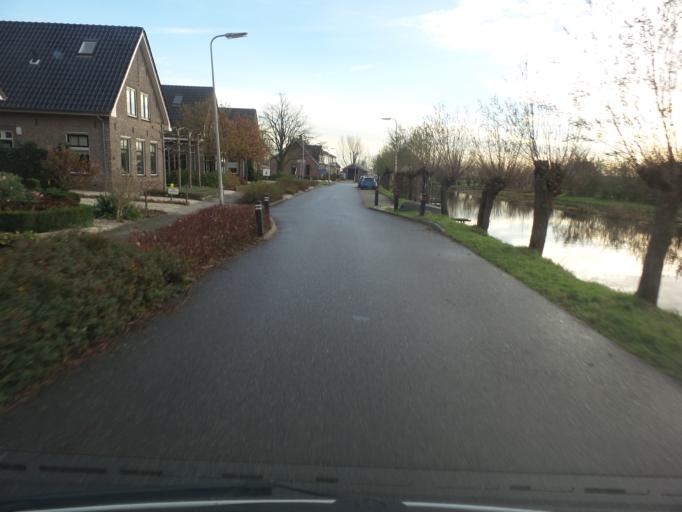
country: NL
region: Utrecht
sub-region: Gemeente Oudewater
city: Oudewater
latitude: 52.0580
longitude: 4.8230
